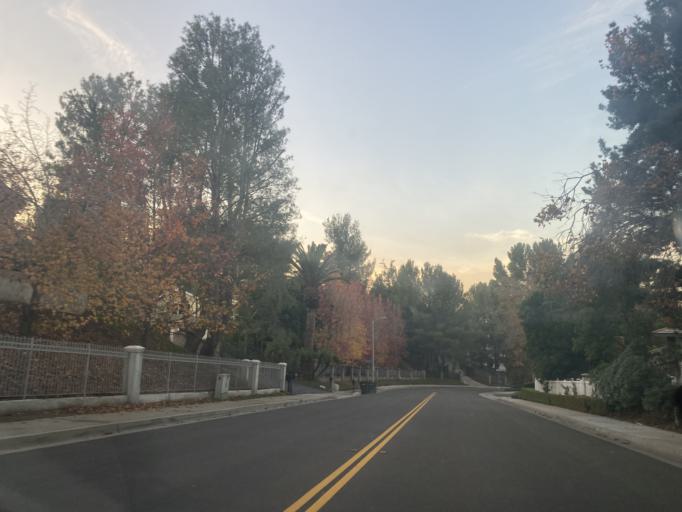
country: US
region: California
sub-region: Orange County
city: North Tustin
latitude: 33.7932
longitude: -117.7771
